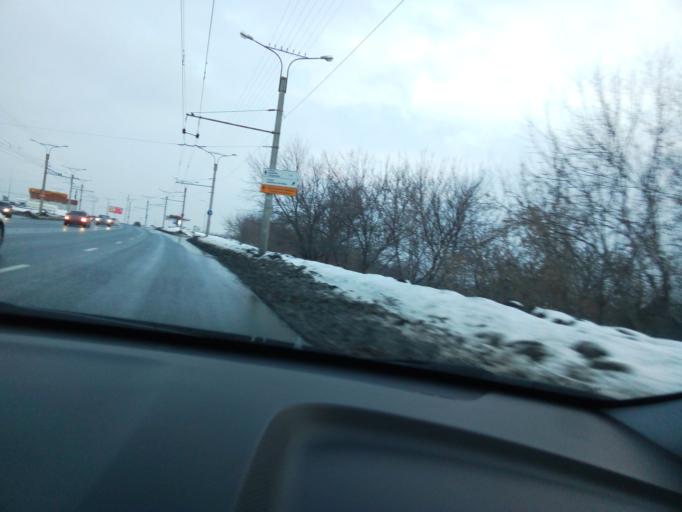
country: RU
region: Chuvashia
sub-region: Cheboksarskiy Rayon
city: Cheboksary
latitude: 56.1254
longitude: 47.2442
